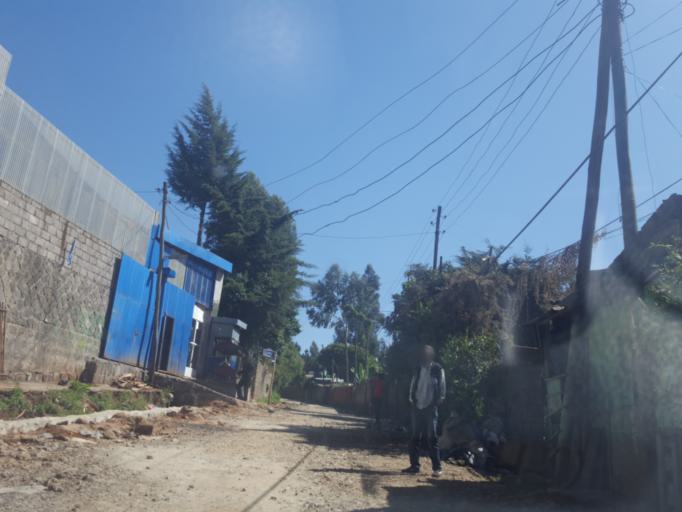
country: ET
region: Adis Abeba
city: Addis Ababa
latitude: 9.0632
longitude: 38.7394
